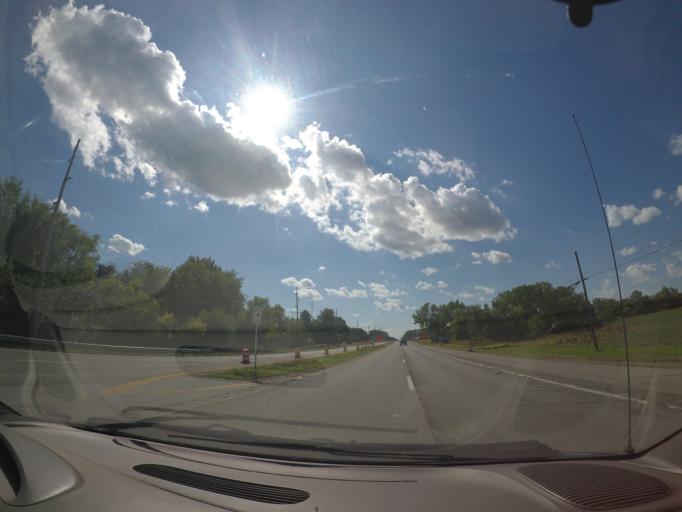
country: US
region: Ohio
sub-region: Sandusky County
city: Green Springs
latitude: 41.3295
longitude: -83.0468
